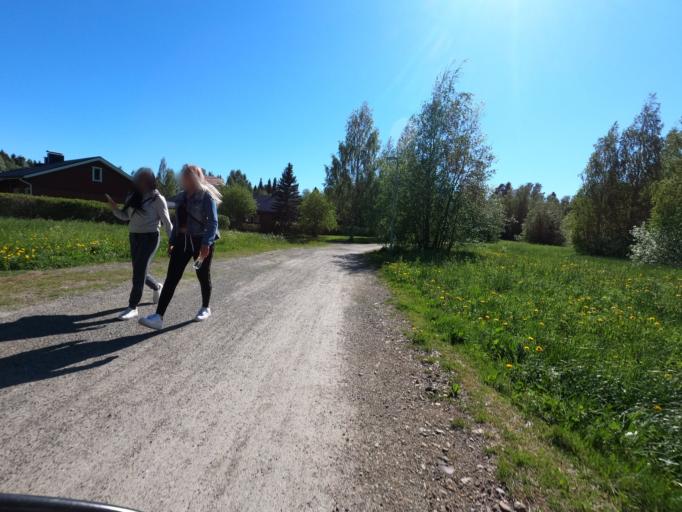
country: FI
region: North Karelia
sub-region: Joensuu
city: Joensuu
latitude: 62.5886
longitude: 29.8001
